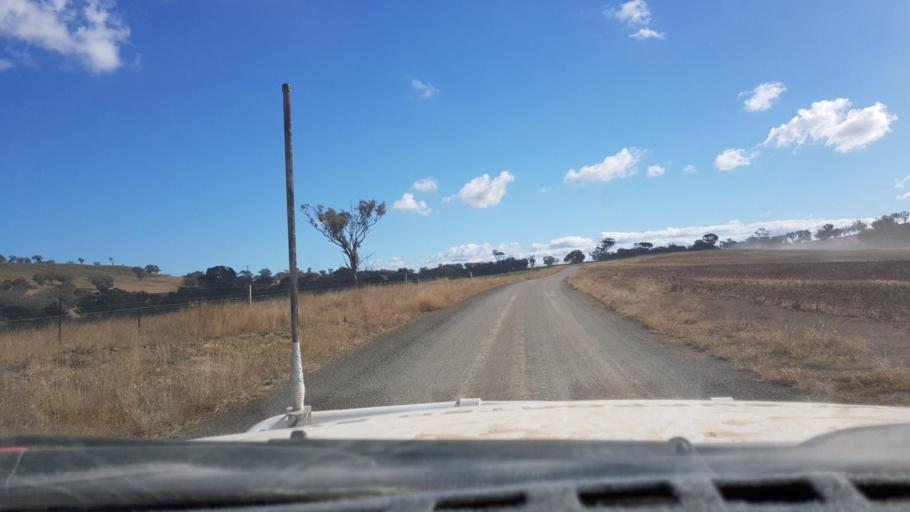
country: AU
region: New South Wales
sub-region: Narrabri
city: Blair Athol
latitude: -30.5605
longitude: 150.4637
